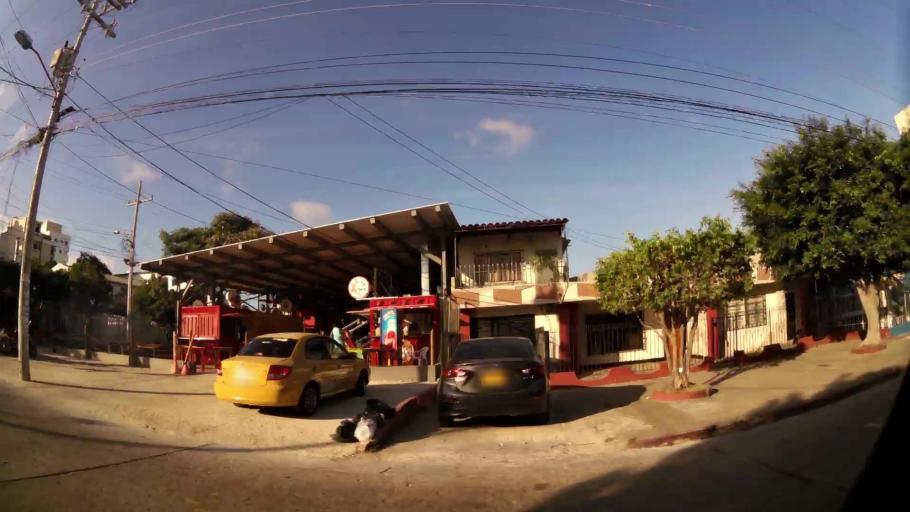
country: CO
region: Atlantico
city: Barranquilla
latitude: 10.9859
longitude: -74.8007
